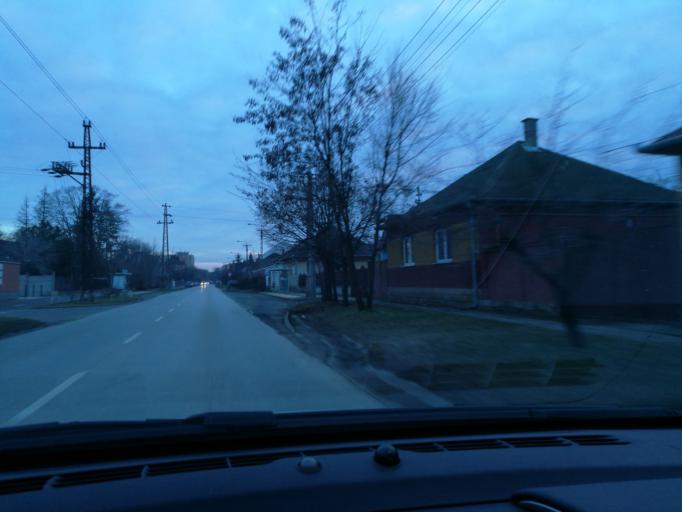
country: HU
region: Szabolcs-Szatmar-Bereg
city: Nyiregyhaza
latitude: 47.9726
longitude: 21.7073
